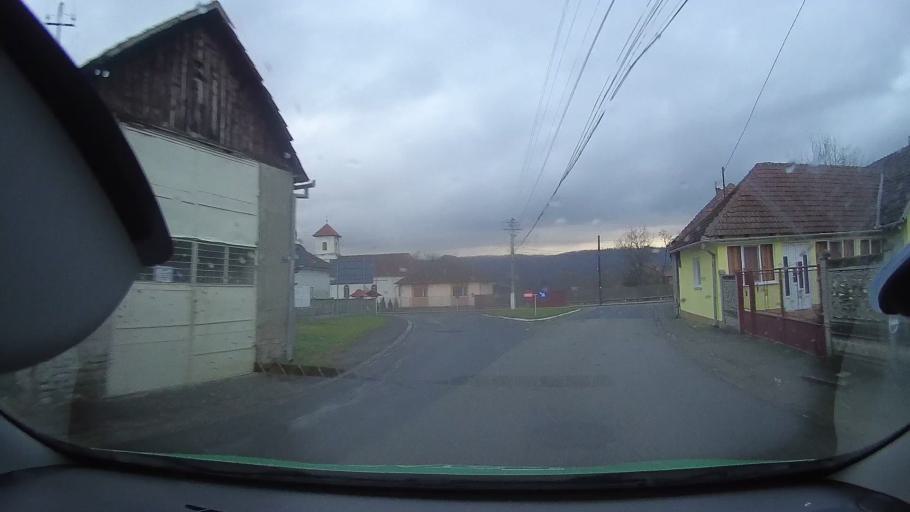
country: RO
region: Hunedoara
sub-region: Comuna Baia de Cris
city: Baia de Cris
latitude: 46.1730
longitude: 22.7152
